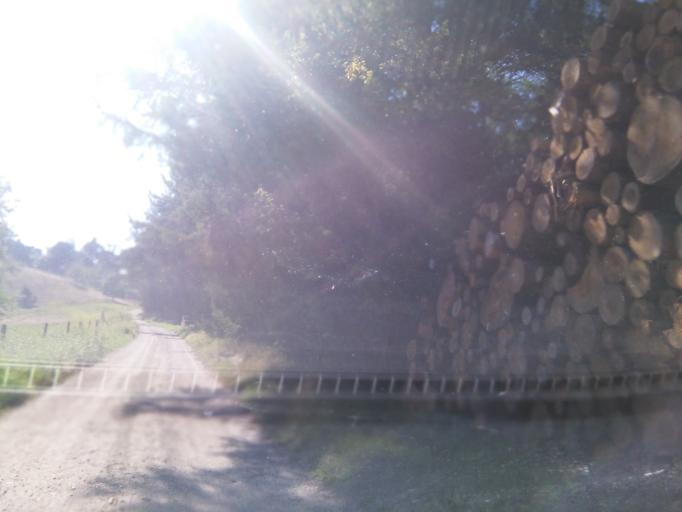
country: DK
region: Central Jutland
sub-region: Syddjurs Kommune
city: Ronde
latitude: 56.2078
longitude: 10.5223
